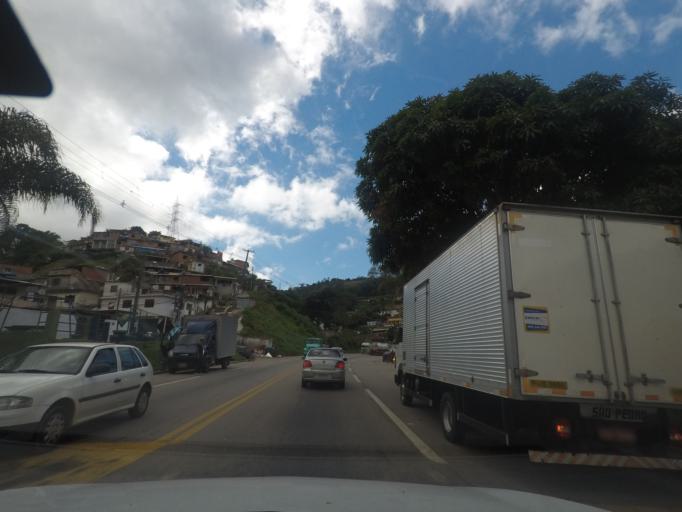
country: BR
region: Rio de Janeiro
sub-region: Teresopolis
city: Teresopolis
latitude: -22.3938
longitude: -42.9528
